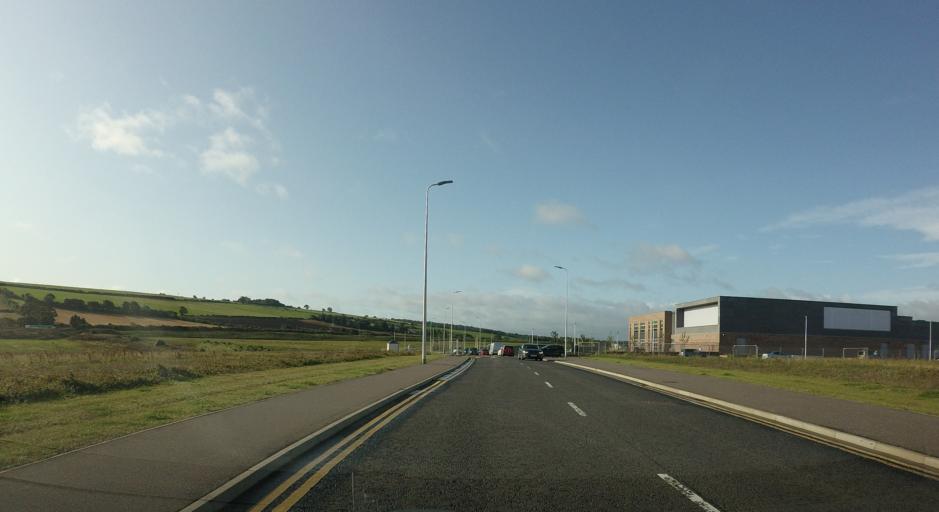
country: GB
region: Scotland
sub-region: East Lothian
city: Prestonpans
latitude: 55.9386
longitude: -3.0029
